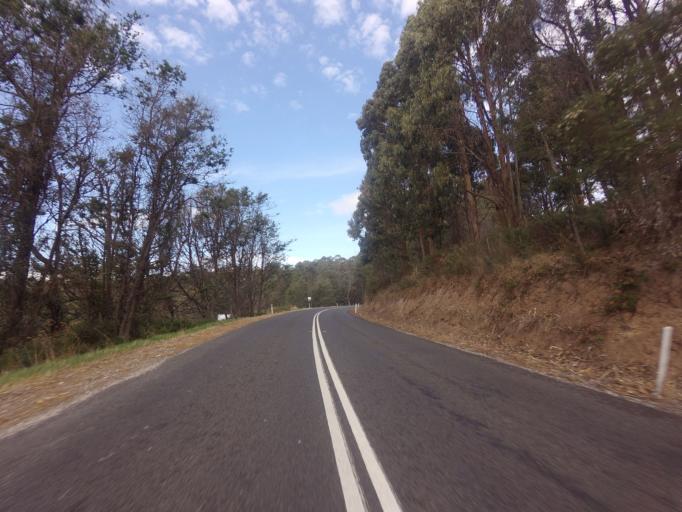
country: AU
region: Tasmania
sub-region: Meander Valley
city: Deloraine
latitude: -41.6364
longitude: 146.7137
